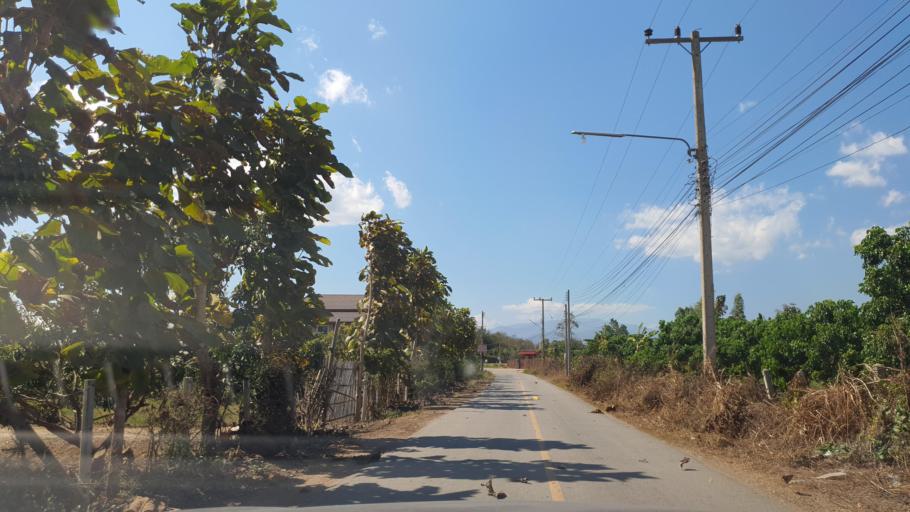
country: TH
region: Chiang Mai
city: Doi Lo
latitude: 18.5324
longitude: 98.8220
